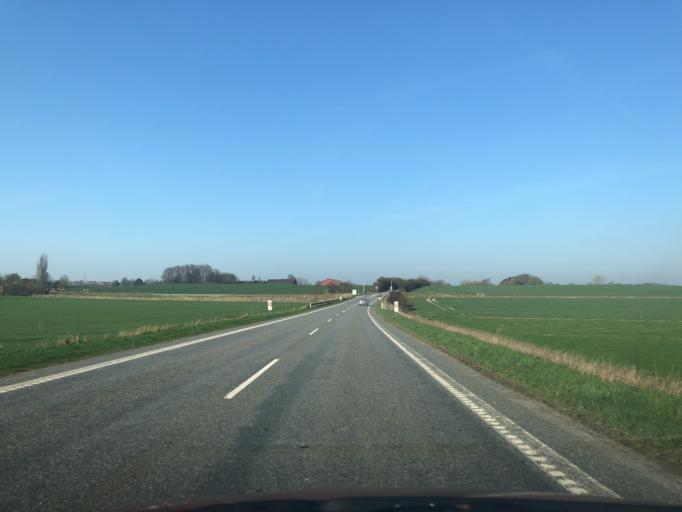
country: DK
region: Zealand
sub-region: Faxe Kommune
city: Fakse
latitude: 55.2719
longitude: 12.1423
